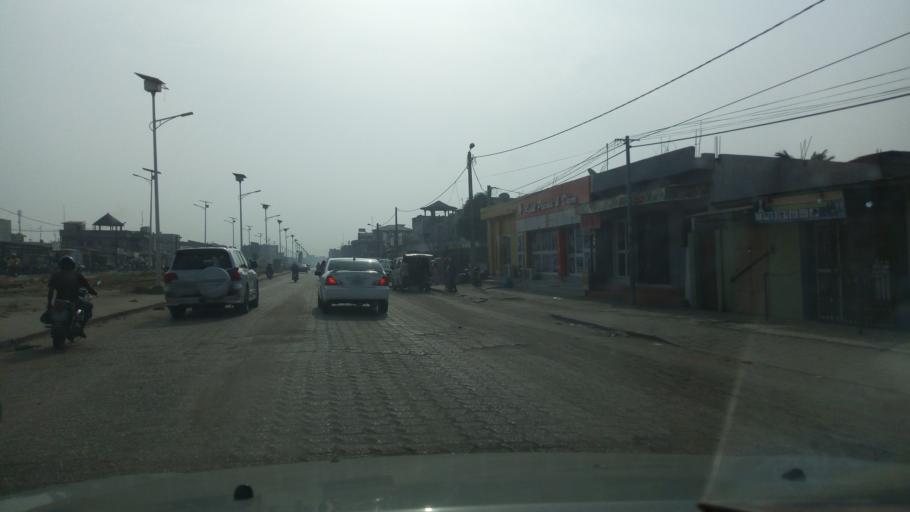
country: BJ
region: Littoral
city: Cotonou
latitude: 6.3757
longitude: 2.3482
